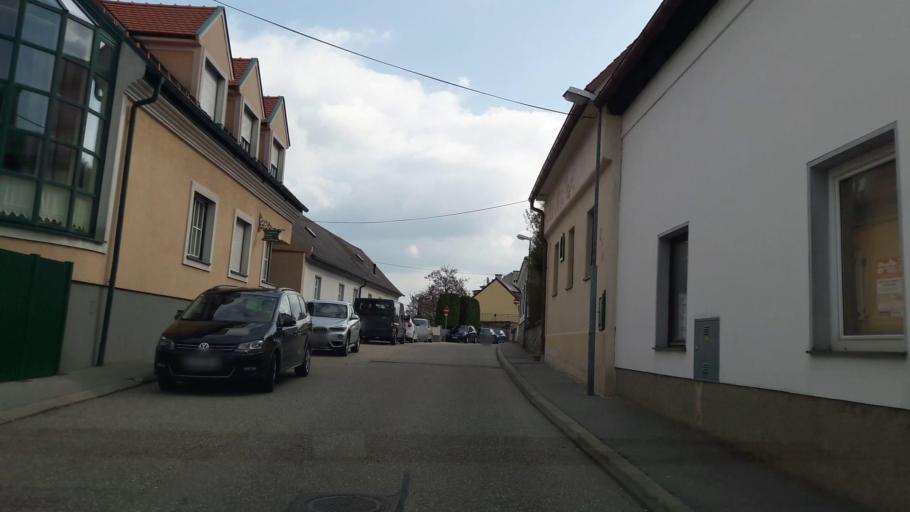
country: AT
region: Lower Austria
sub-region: Politischer Bezirk Bruck an der Leitha
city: Hainburg an der Donau
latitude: 48.1449
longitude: 16.9443
